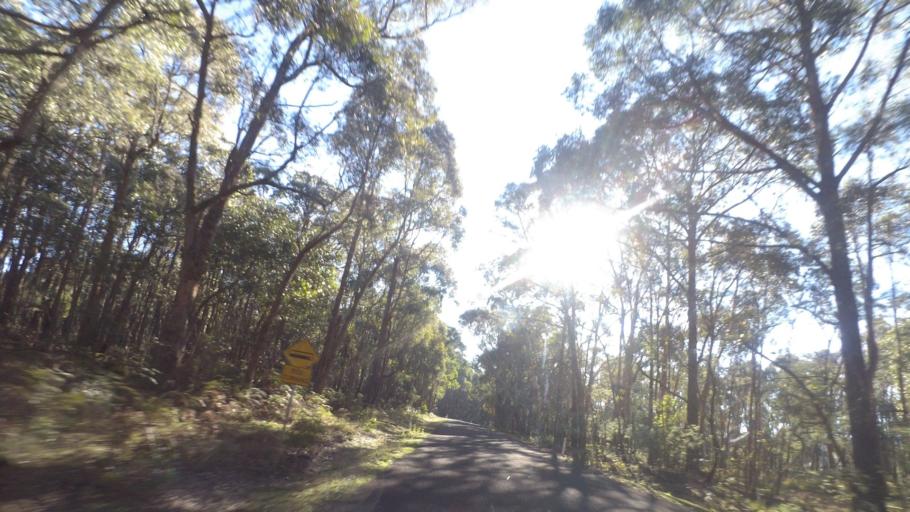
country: AU
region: Victoria
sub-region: Mount Alexander
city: Castlemaine
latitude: -37.3280
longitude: 144.3184
